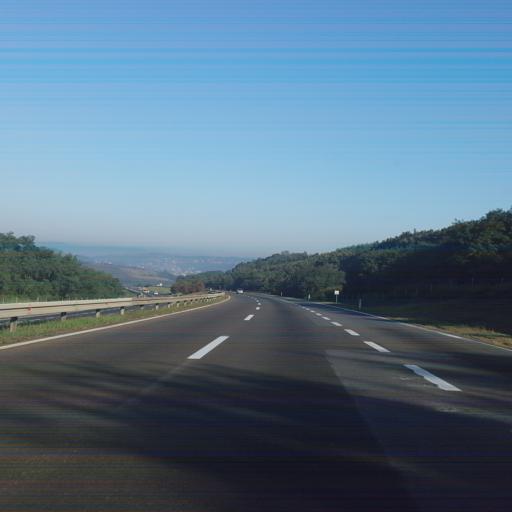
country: RS
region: Central Serbia
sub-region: Belgrade
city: Grocka
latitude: 44.6359
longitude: 20.6363
